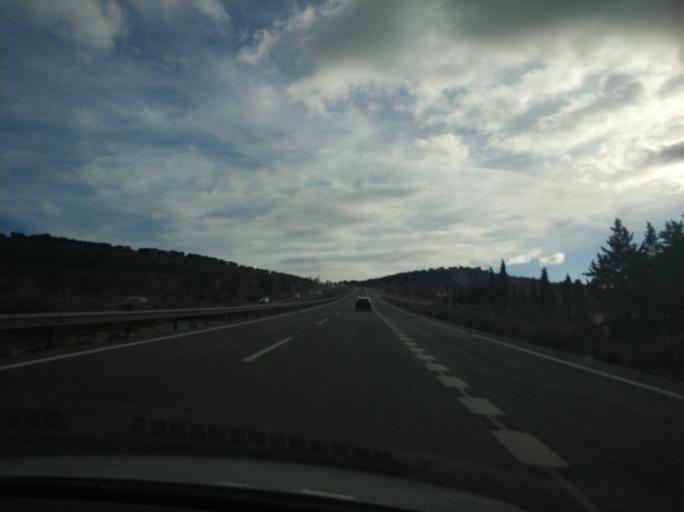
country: ES
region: Madrid
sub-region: Provincia de Madrid
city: Buitrago del Lozoya
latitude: 40.9640
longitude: -3.6417
